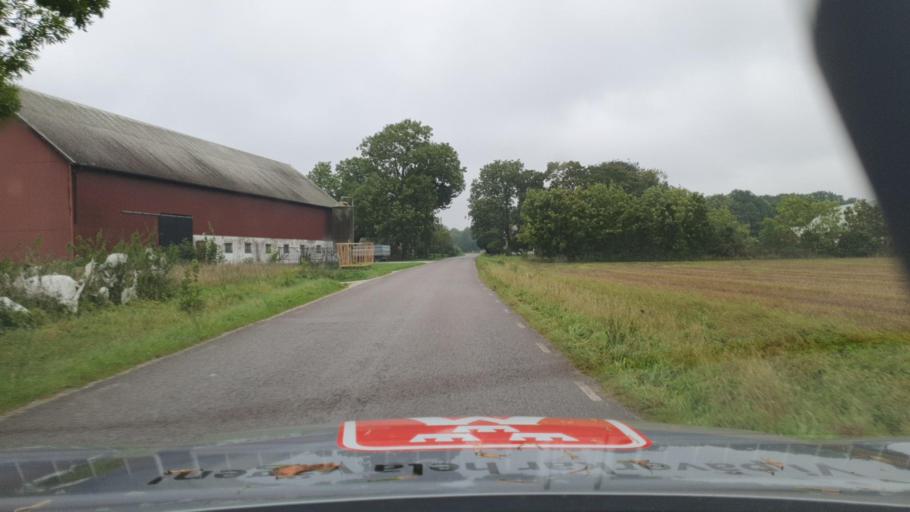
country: SE
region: Gotland
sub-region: Gotland
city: Visby
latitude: 57.7809
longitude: 18.5095
